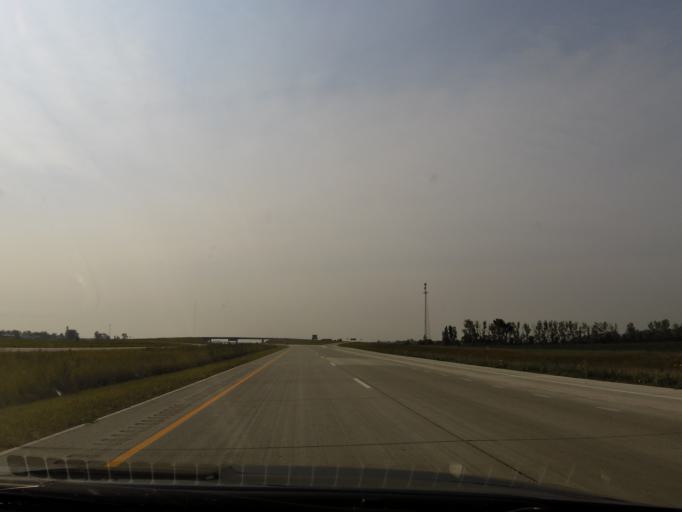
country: US
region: North Dakota
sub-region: Traill County
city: Hillsboro
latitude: 47.1570
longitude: -96.9755
